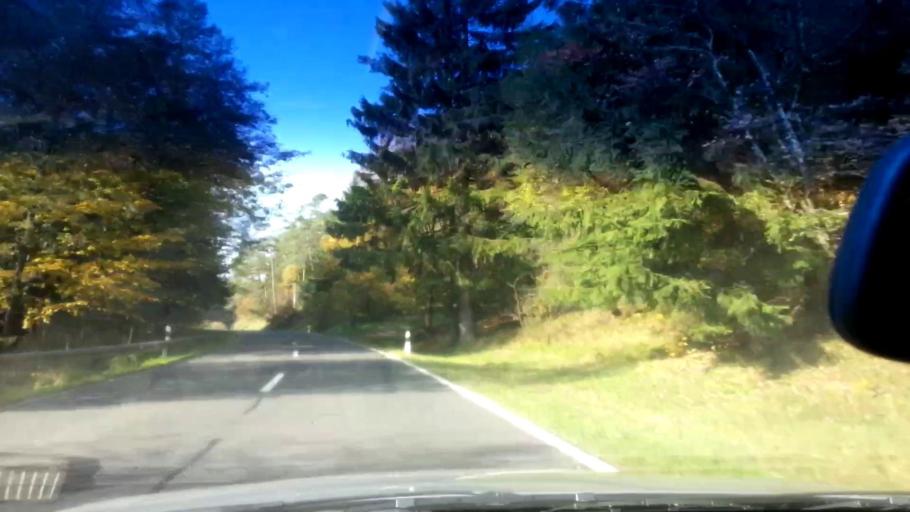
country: DE
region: Bavaria
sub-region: Upper Franconia
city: Stadelhofen
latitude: 49.9581
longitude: 11.2117
